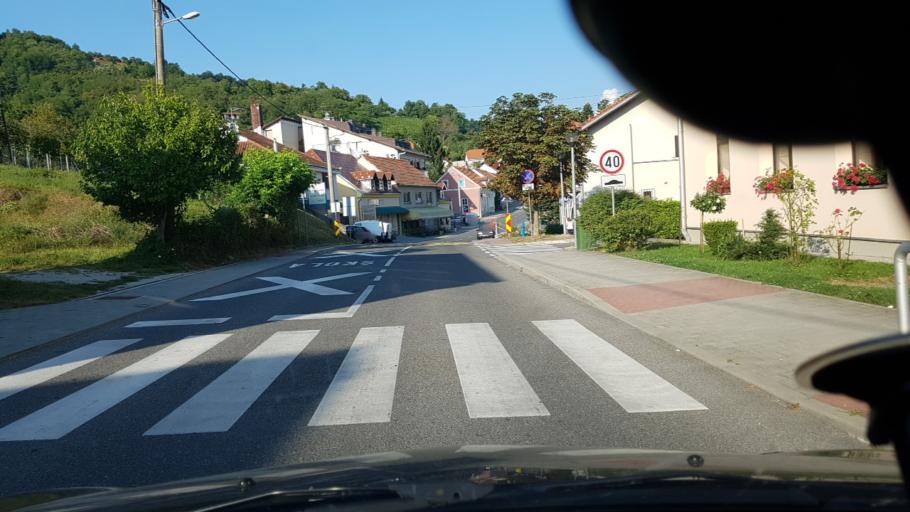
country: SI
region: Bistrica ob Sotli
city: Bistrica ob Sotli
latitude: 46.0494
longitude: 15.7388
